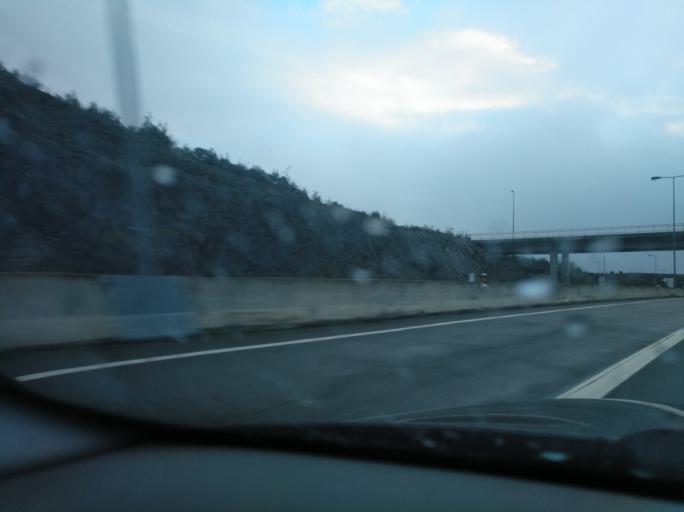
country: PT
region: Faro
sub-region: Castro Marim
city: Castro Marim
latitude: 37.3165
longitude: -7.4867
